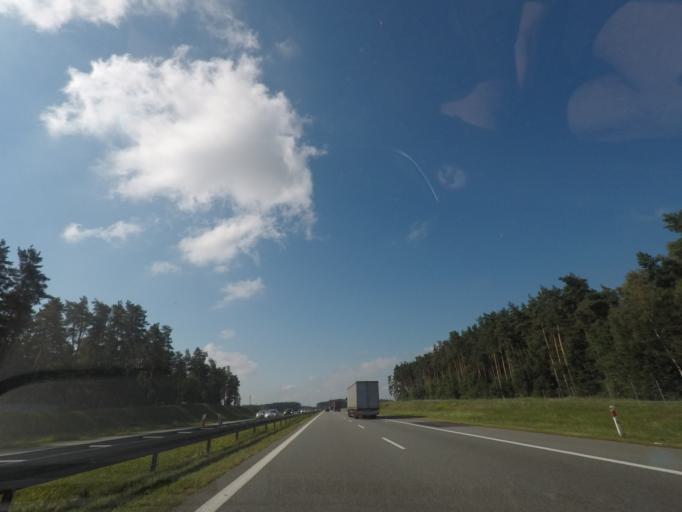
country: PL
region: Pomeranian Voivodeship
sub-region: Powiat tczewski
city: Pelplin
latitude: 54.0117
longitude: 18.6615
